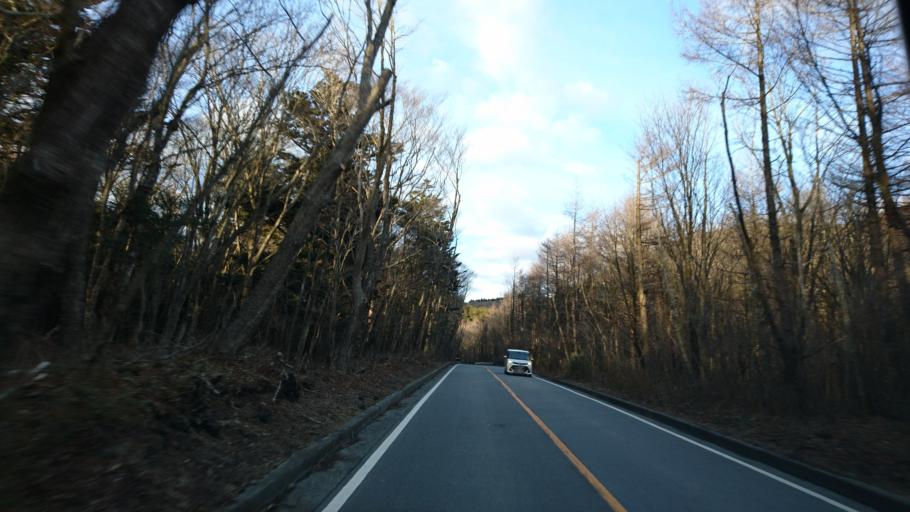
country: JP
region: Yamanashi
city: Fujikawaguchiko
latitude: 35.4351
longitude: 138.6382
